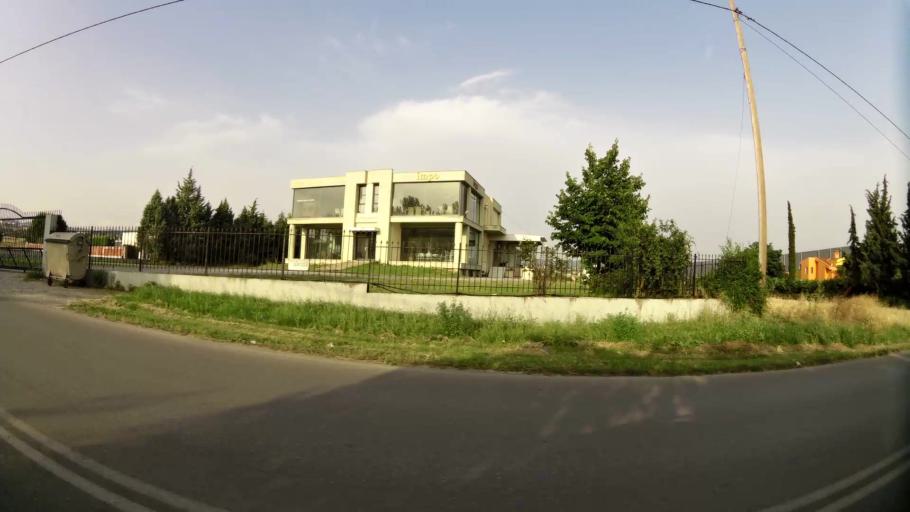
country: GR
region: Central Macedonia
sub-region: Nomos Thessalonikis
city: Oraiokastro
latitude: 40.7069
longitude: 22.9123
